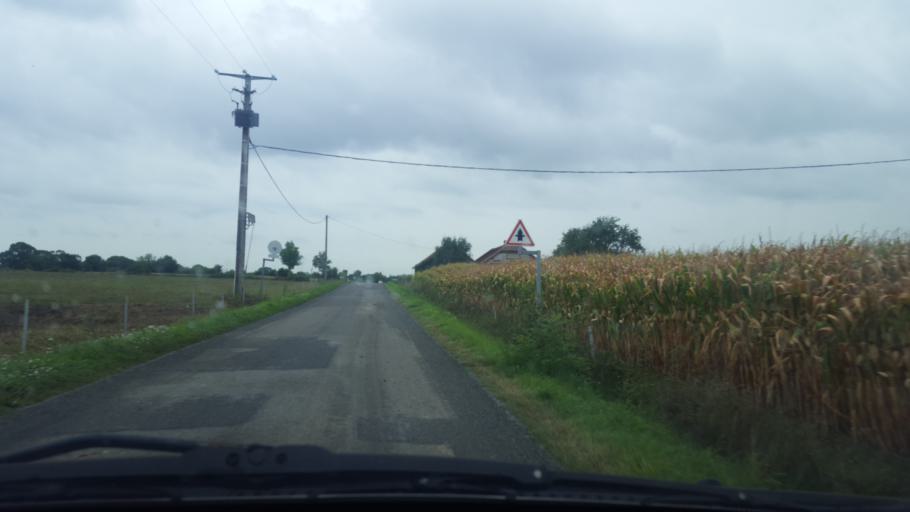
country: FR
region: Pays de la Loire
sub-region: Departement de la Loire-Atlantique
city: Saint-Philbert-de-Grand-Lieu
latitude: 47.0466
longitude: -1.6834
